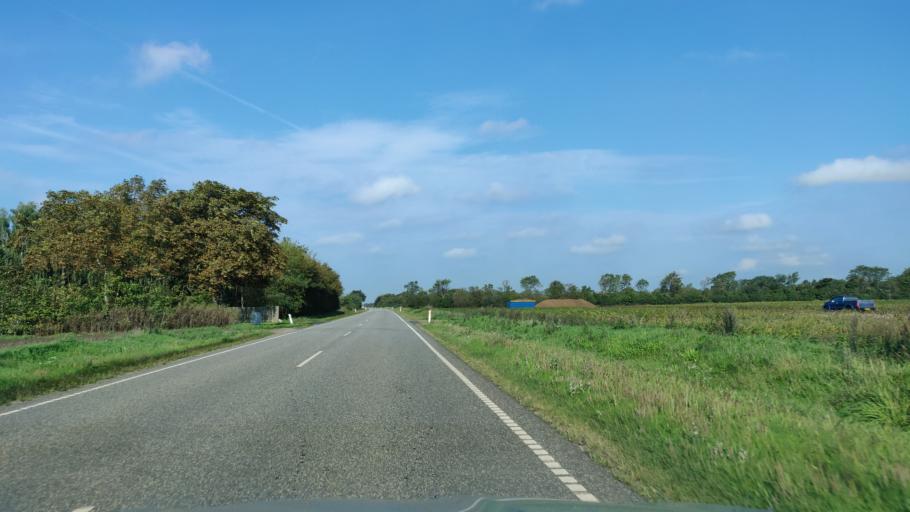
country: DK
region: Central Jutland
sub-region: Herning Kommune
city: Sunds
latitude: 56.2545
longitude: 9.0478
